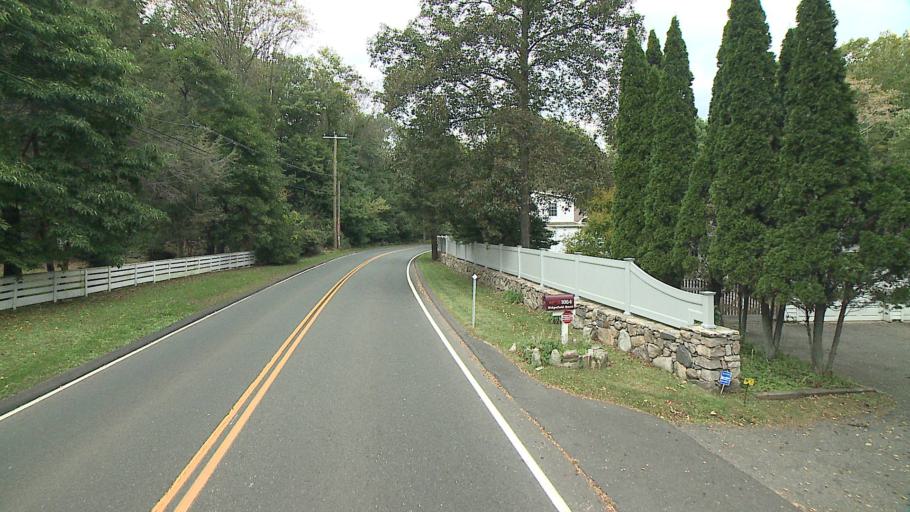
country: US
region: Connecticut
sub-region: Fairfield County
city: Ridgefield
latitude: 41.2418
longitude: -73.4858
